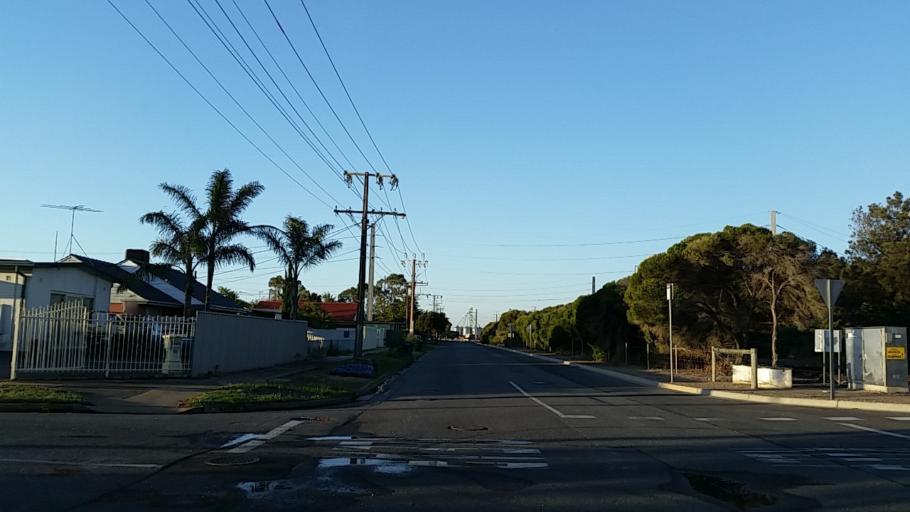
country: AU
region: South Australia
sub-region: Port Adelaide Enfield
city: Birkenhead
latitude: -34.7983
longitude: 138.5048
